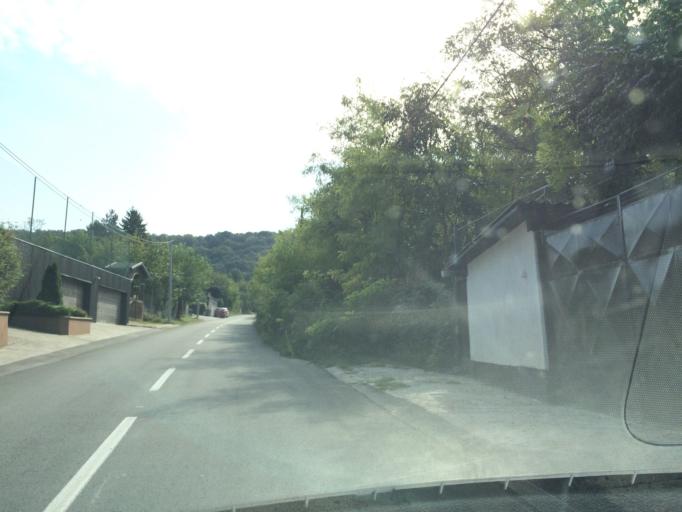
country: RS
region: Autonomna Pokrajina Vojvodina
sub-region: Juznobacki Okrug
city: Novi Sad
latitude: 45.1862
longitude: 19.8283
